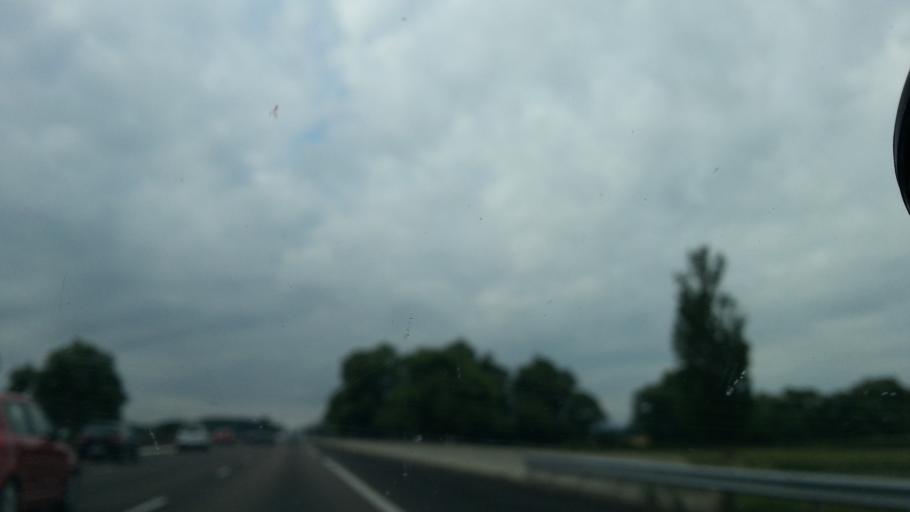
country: FR
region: Bourgogne
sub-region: Departement de Saone-et-Loire
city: Demigny
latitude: 46.9349
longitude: 4.8226
